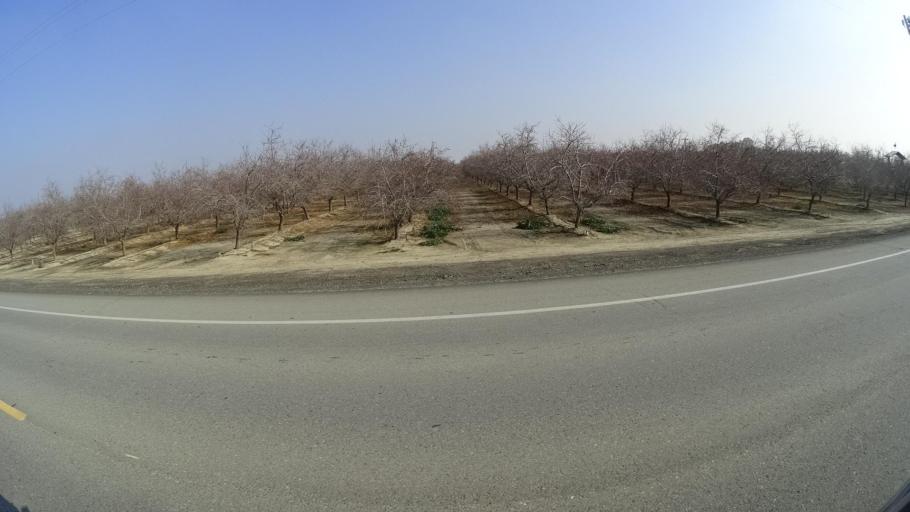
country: US
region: California
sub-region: Kern County
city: Greenfield
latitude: 35.2132
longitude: -119.1100
